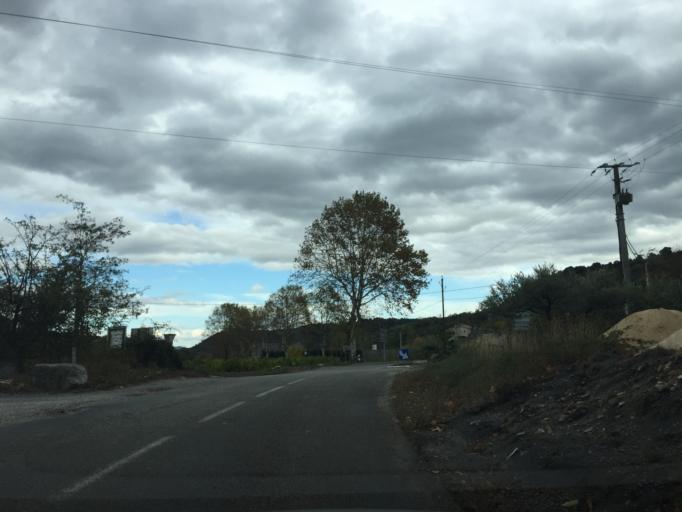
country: FR
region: Rhone-Alpes
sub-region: Departement de l'Ardeche
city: Les Vans
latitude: 44.4092
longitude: 4.1101
